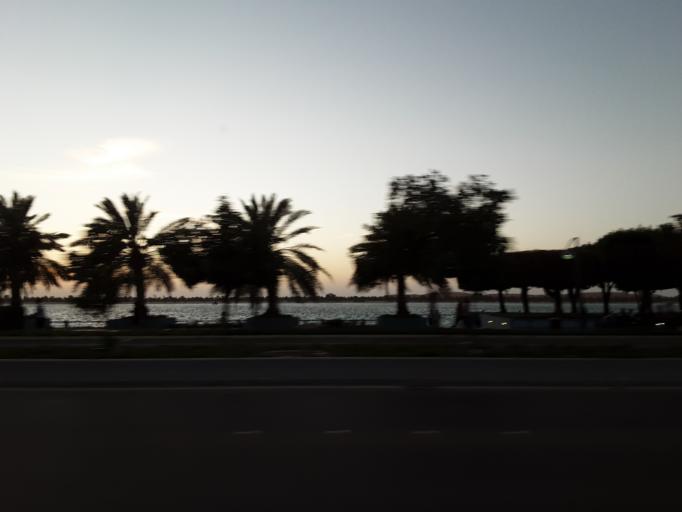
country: AE
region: Abu Dhabi
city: Abu Dhabi
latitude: 24.4931
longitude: 54.3551
